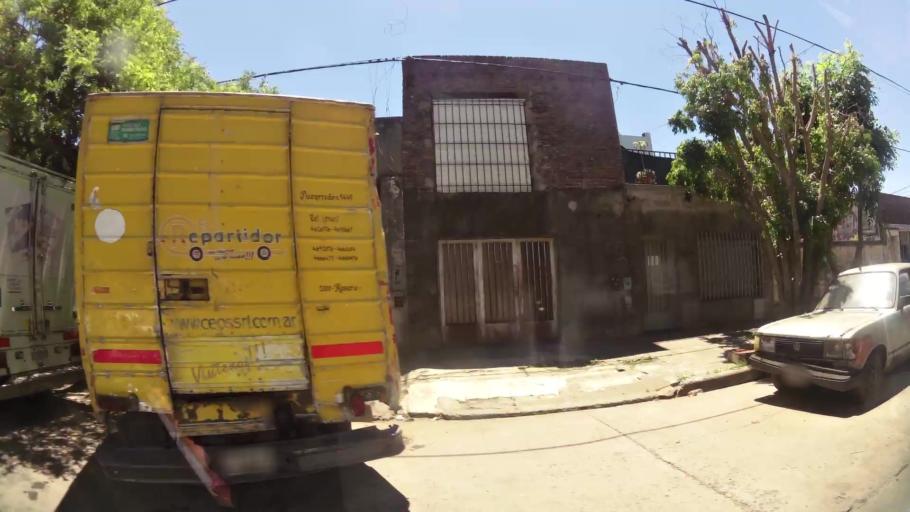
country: AR
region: Santa Fe
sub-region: Departamento de Rosario
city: Rosario
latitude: -32.9432
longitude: -60.7001
